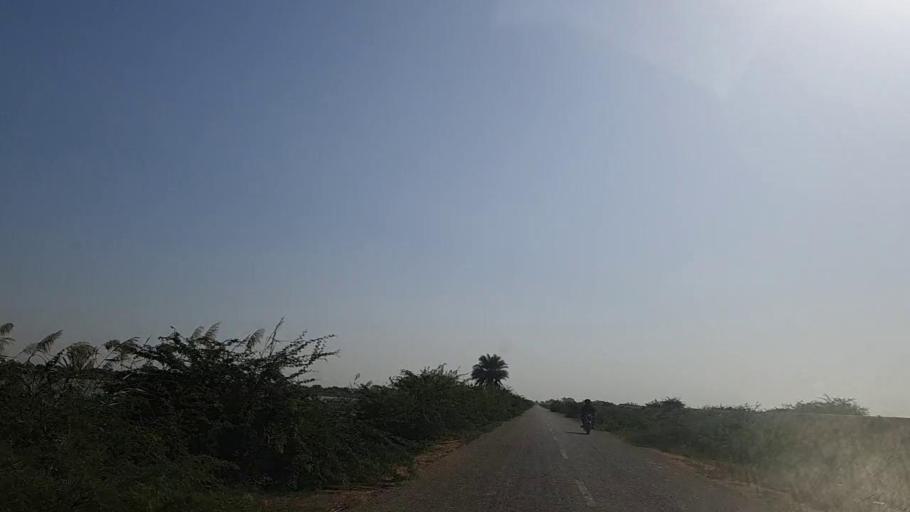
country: PK
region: Sindh
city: Jati
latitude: 24.4369
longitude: 68.2604
